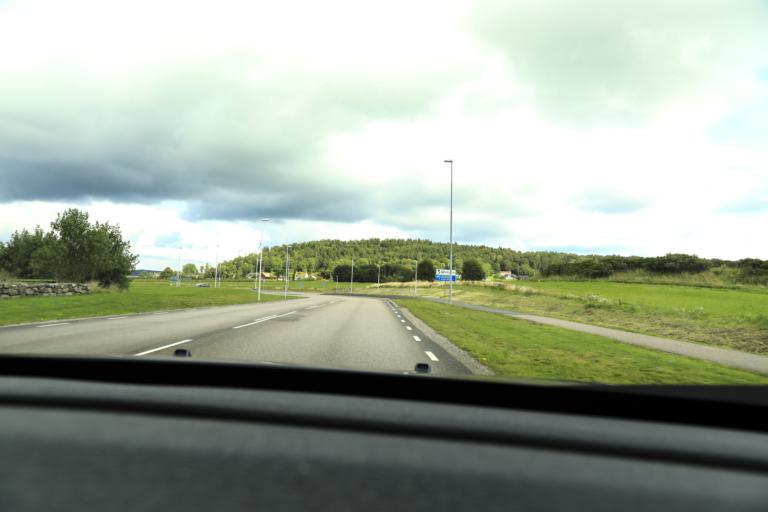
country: SE
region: Halland
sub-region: Kungsbacka Kommun
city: Kungsbacka
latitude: 57.5114
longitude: 12.0843
